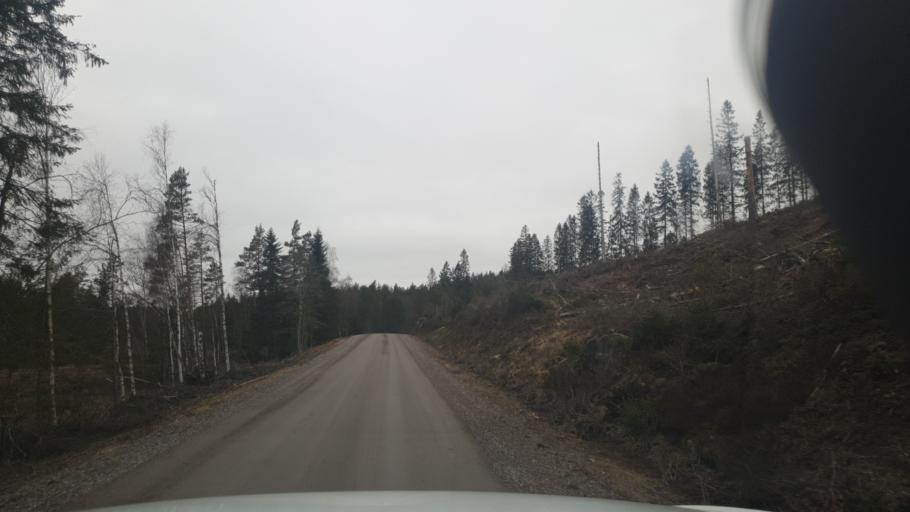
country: NO
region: Ostfold
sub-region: Romskog
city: Romskog
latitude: 59.7086
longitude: 12.0407
